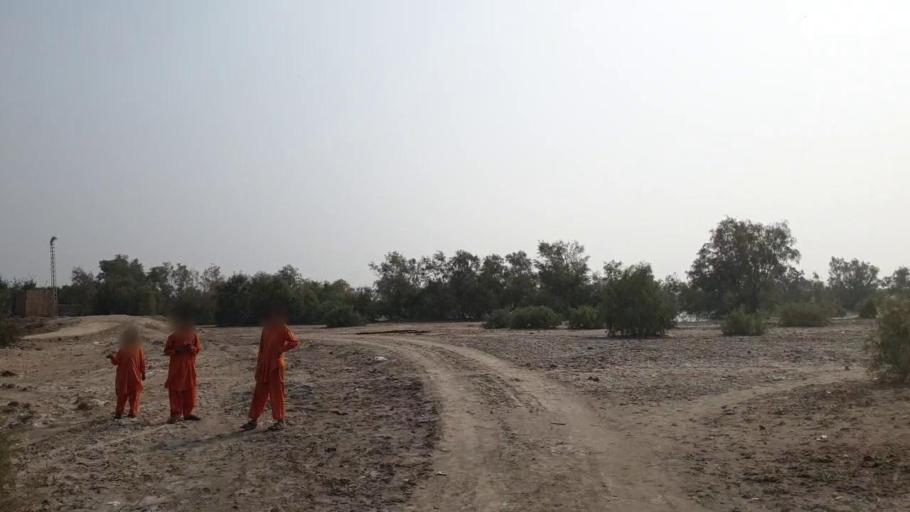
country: PK
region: Sindh
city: Bhan
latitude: 26.5076
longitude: 67.6736
